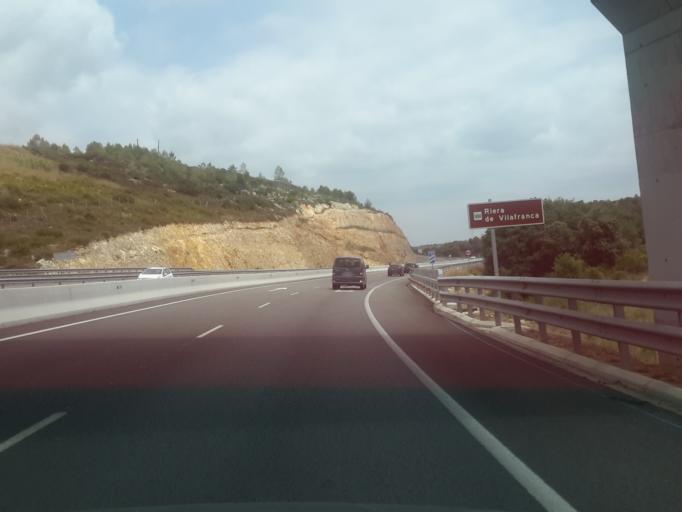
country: ES
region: Catalonia
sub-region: Provincia de Barcelona
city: Vilafranca del Penedes
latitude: 41.3166
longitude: 1.7247
